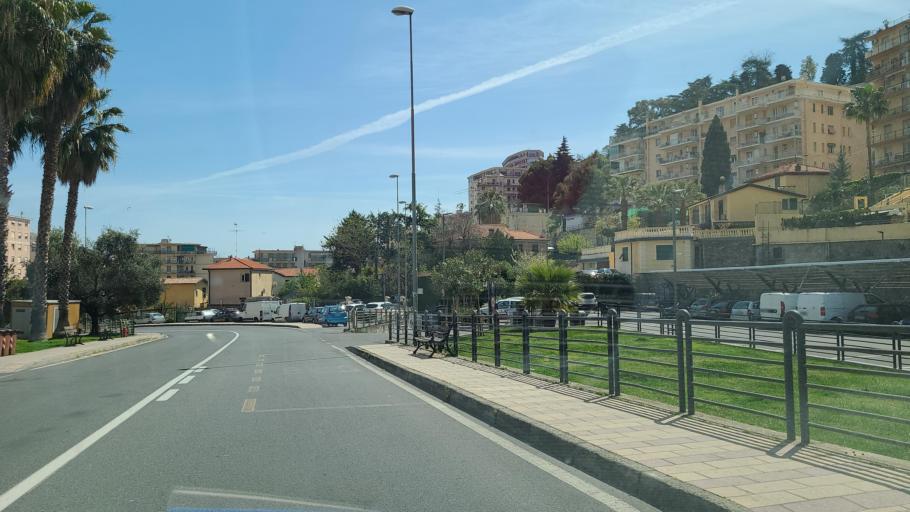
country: IT
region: Liguria
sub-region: Provincia di Imperia
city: San Remo
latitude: 43.8233
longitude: 7.7651
